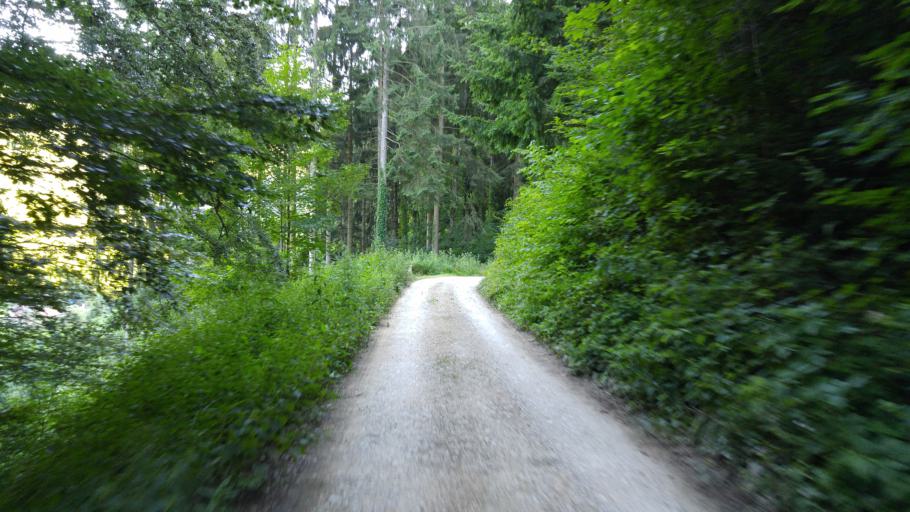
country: DE
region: Baden-Wuerttemberg
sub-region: Freiburg Region
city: Muenstertal/Schwarzwald
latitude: 47.8411
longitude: 7.7909
